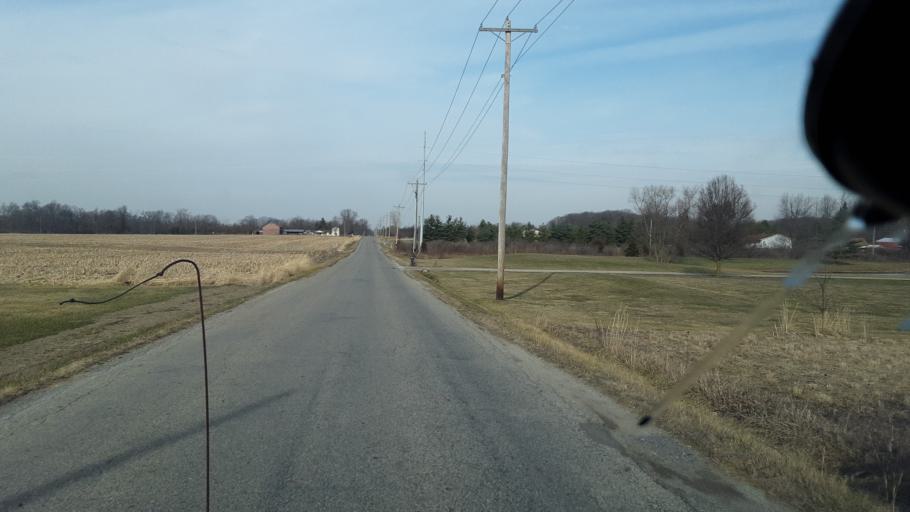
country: US
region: Indiana
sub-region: DeKalb County
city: Butler
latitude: 41.3874
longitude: -84.8889
